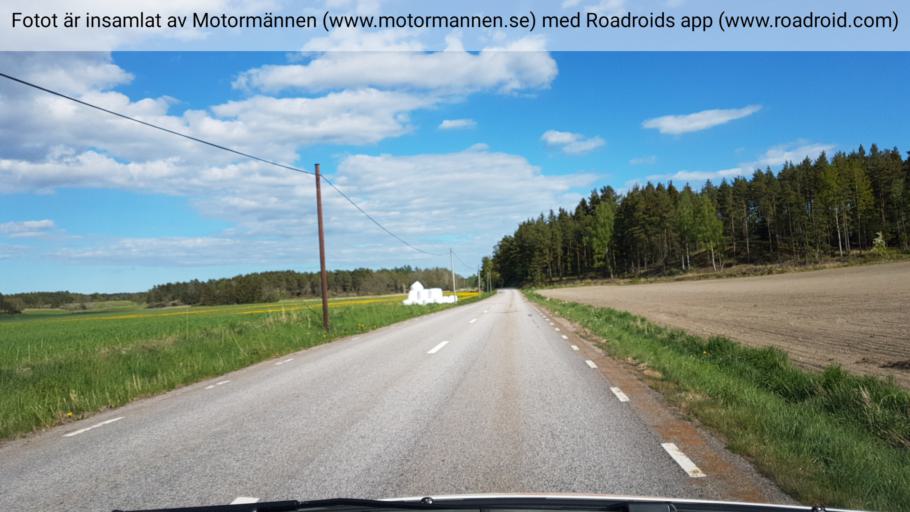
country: SE
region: Kalmar
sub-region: Vasterviks Kommun
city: Forserum
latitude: 57.9290
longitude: 16.5269
